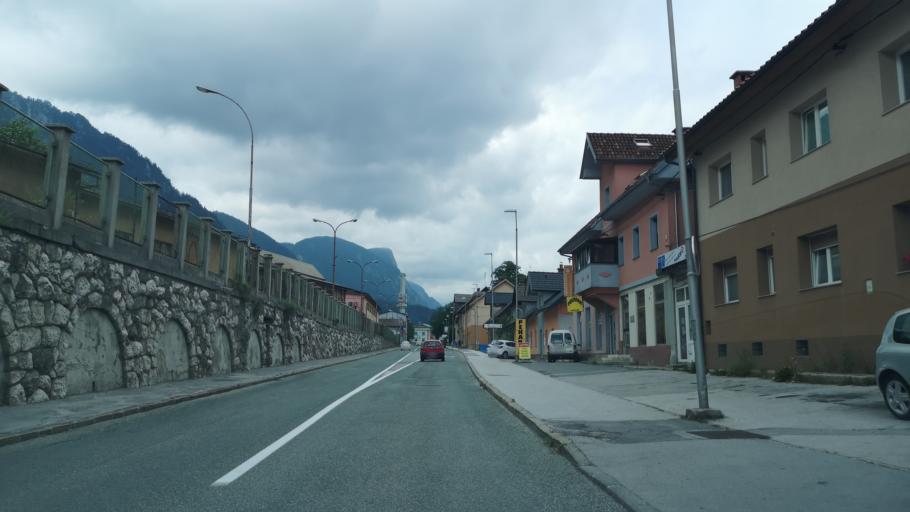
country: SI
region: Jesenice
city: Jesenice
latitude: 46.4310
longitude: 14.0690
